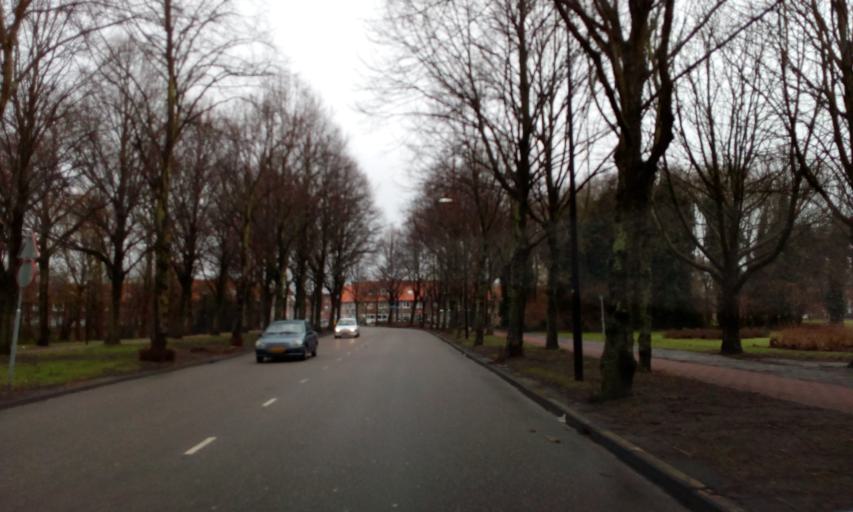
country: NL
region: South Holland
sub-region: Gemeente Rijswijk
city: Rijswijk
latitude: 52.0493
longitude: 4.3146
